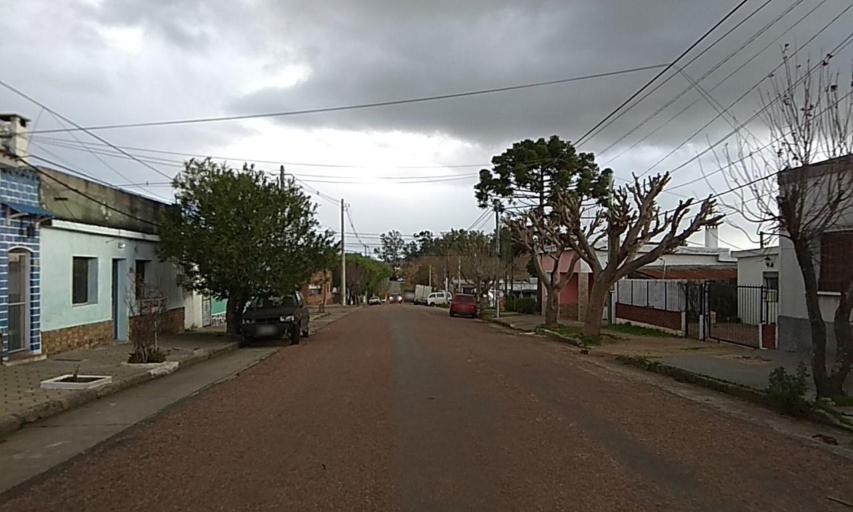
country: UY
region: Florida
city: Florida
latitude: -34.1033
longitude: -56.2212
